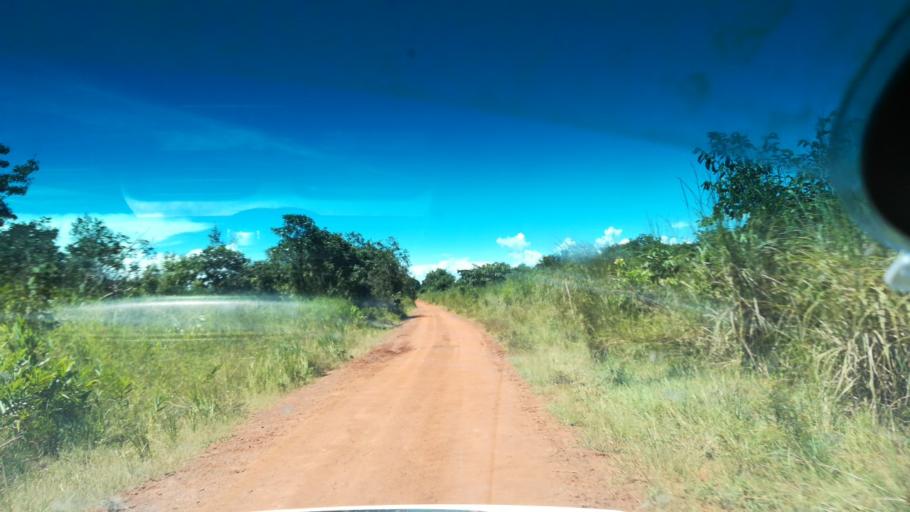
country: ZM
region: Luapula
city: Nchelenge
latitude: -8.6526
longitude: 28.7193
